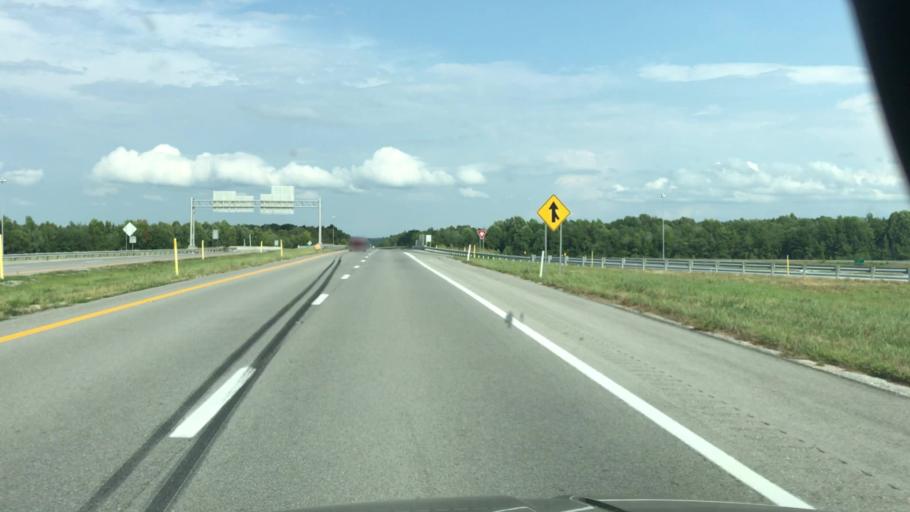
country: US
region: Kentucky
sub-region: Hopkins County
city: Nortonville
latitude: 37.2124
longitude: -87.4433
